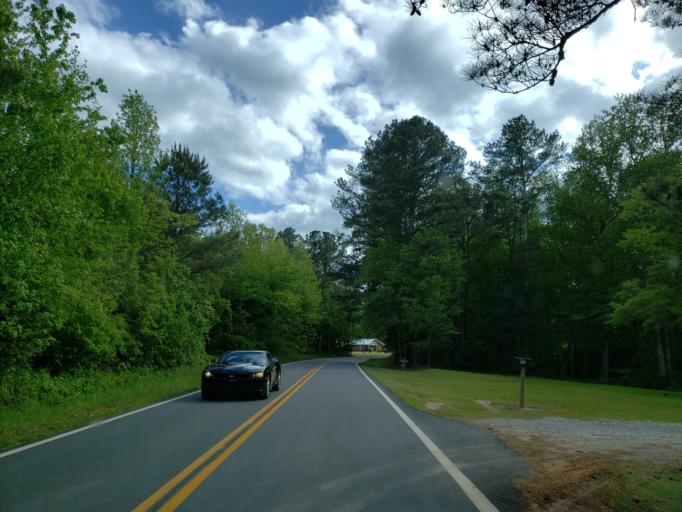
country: US
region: Georgia
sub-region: Carroll County
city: Mount Zion
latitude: 33.6866
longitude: -85.1946
